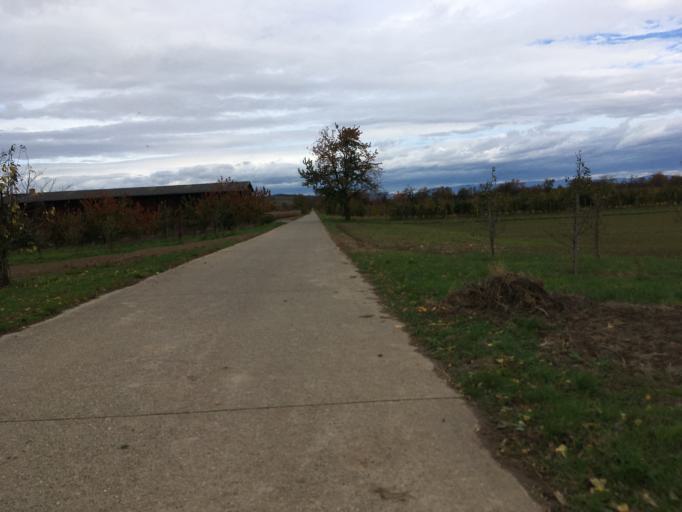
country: DE
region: Baden-Wuerttemberg
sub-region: Freiburg Region
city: Wyhl
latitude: 48.1375
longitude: 7.6520
